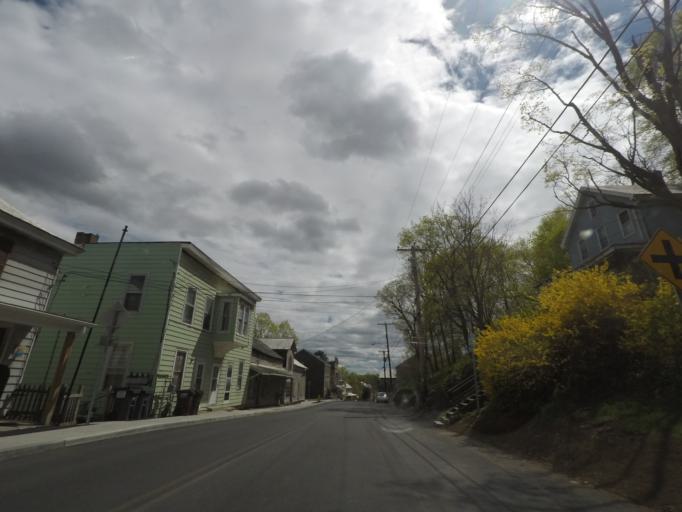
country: US
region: New York
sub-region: Albany County
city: Ravena
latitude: 42.4744
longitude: -73.7927
